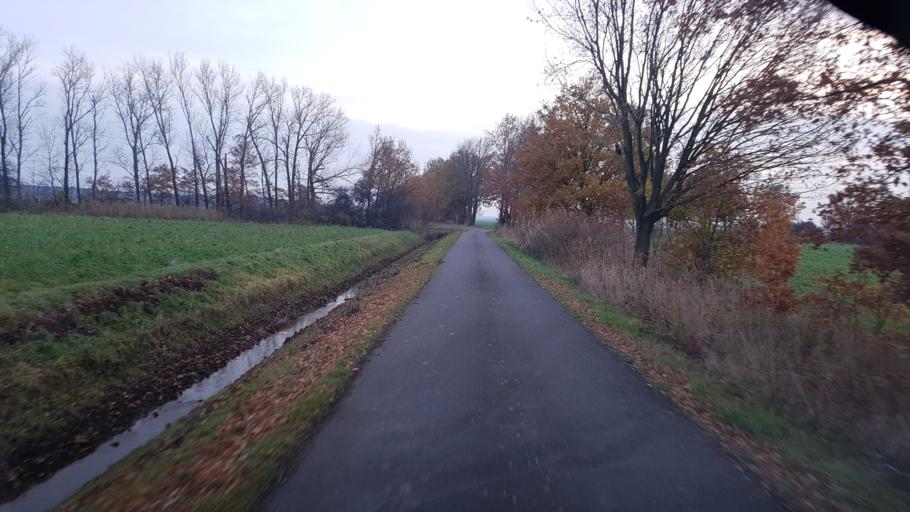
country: DE
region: Brandenburg
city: Vogelsang
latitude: 52.2254
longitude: 14.6659
